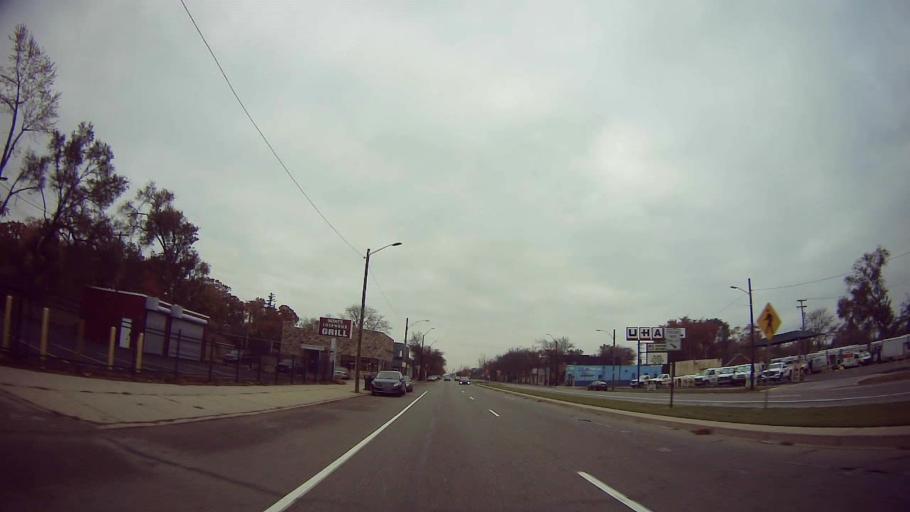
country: US
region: Michigan
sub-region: Oakland County
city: Ferndale
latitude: 42.4377
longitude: -83.1415
